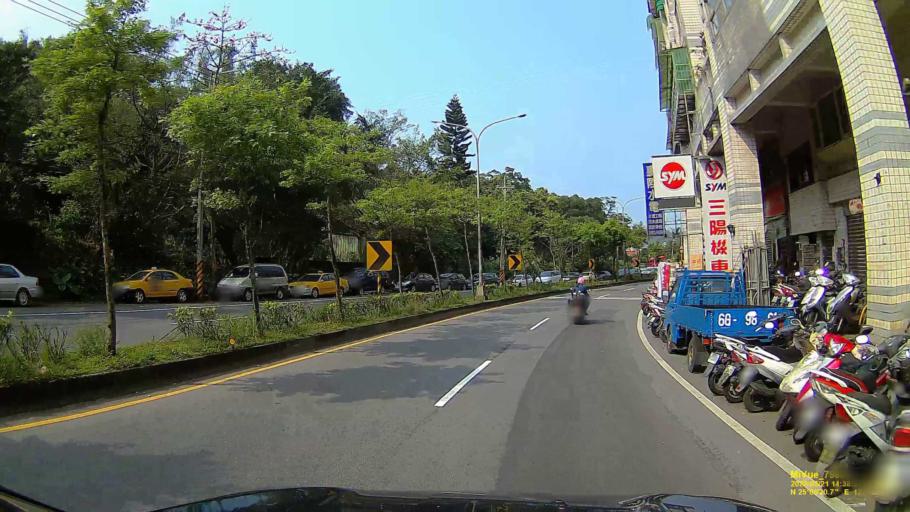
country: TW
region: Taiwan
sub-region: Keelung
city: Keelung
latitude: 25.0892
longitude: 121.7053
